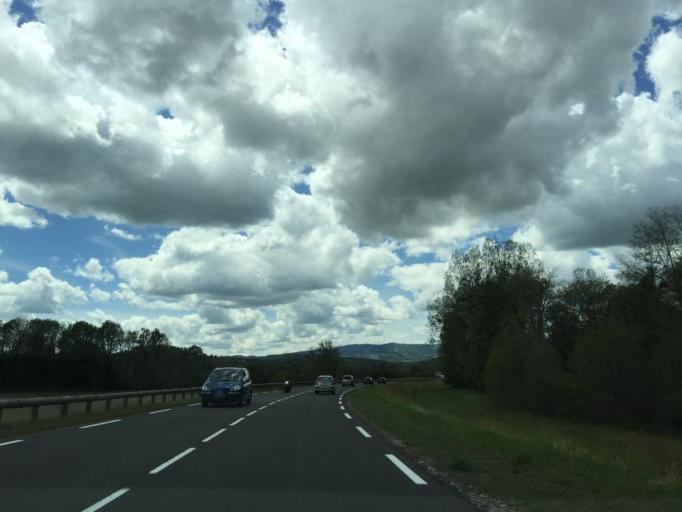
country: FR
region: Rhone-Alpes
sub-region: Departement de la Loire
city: Saint-Marcellin-en-Forez
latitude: 45.5025
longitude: 4.1692
